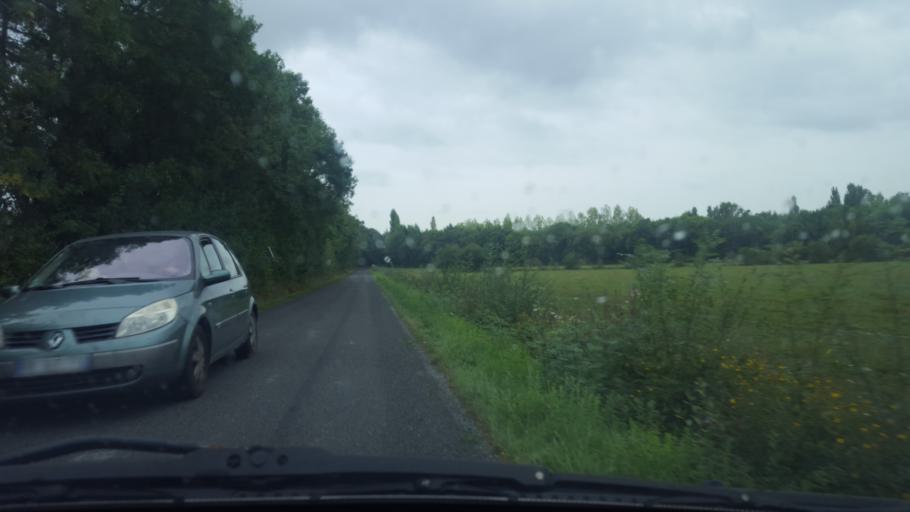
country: FR
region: Pays de la Loire
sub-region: Departement de la Loire-Atlantique
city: Saint-Lumine-de-Coutais
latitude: 47.0491
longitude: -1.6931
